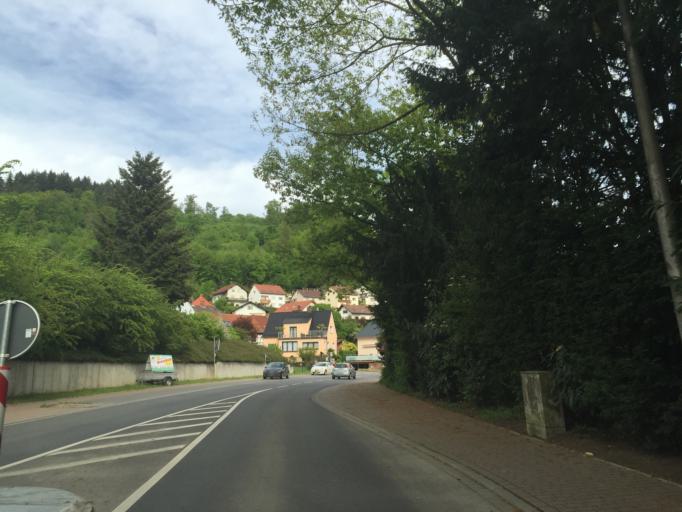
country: DE
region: Hesse
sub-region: Regierungsbezirk Darmstadt
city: Birkenau
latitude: 49.5419
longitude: 8.7051
